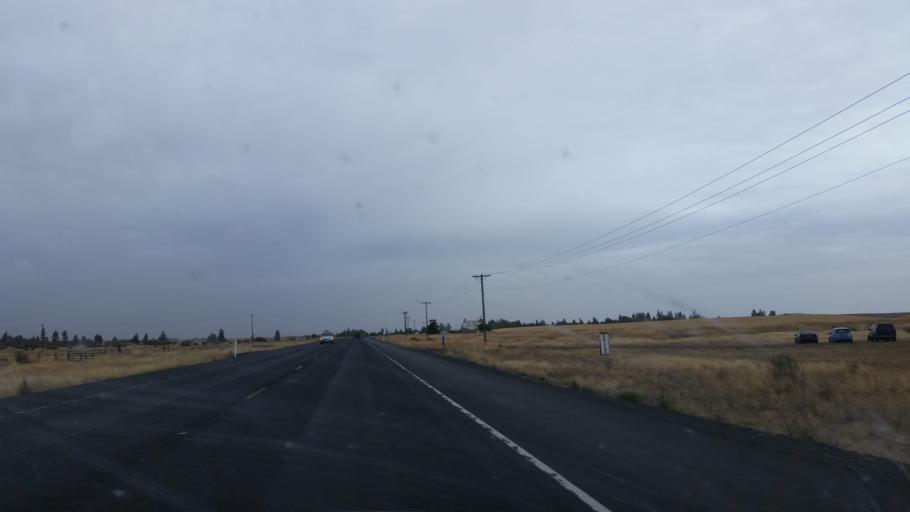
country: US
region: Washington
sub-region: Spokane County
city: Medical Lake
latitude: 47.6675
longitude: -117.9063
